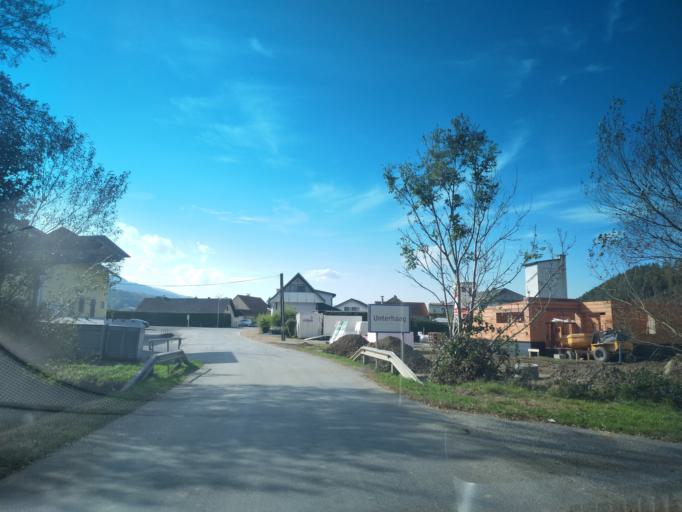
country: AT
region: Styria
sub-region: Politischer Bezirk Leibnitz
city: Oberhaag
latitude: 46.6865
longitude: 15.3577
